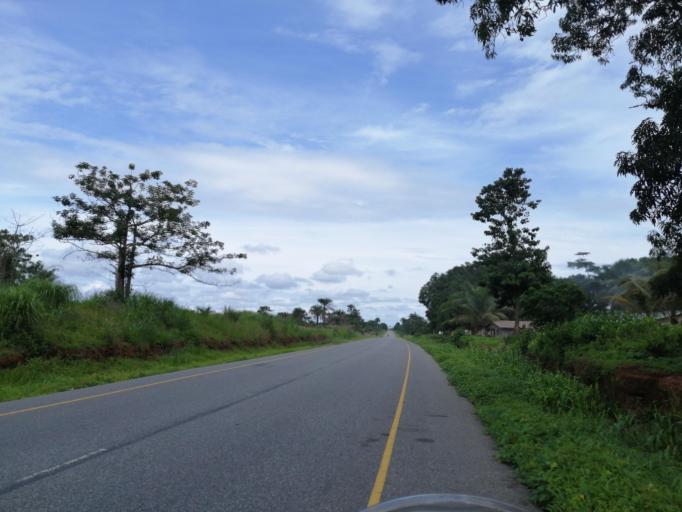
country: SL
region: Northern Province
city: Port Loko
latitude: 8.7415
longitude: -12.9397
